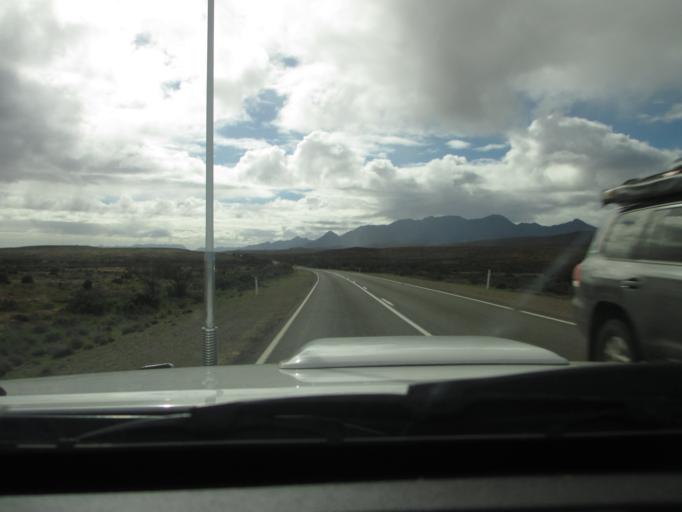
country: AU
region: South Australia
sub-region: Flinders Ranges
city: Quorn
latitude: -31.5916
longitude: 138.4124
